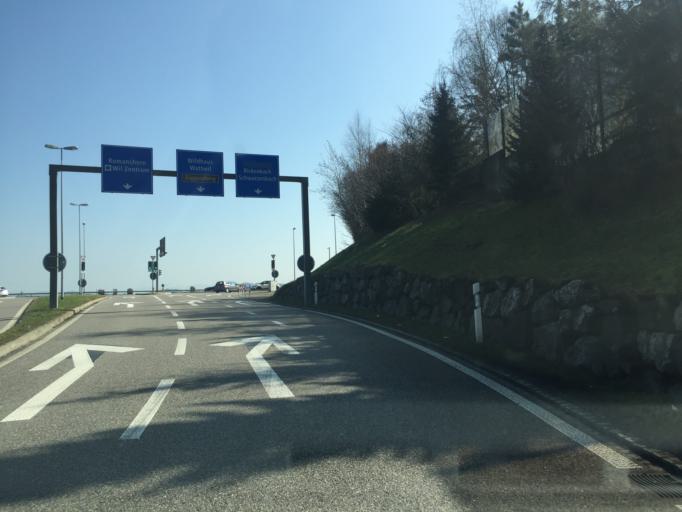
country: CH
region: Saint Gallen
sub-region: Wahlkreis Wil
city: Wil
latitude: 47.4529
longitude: 9.0528
